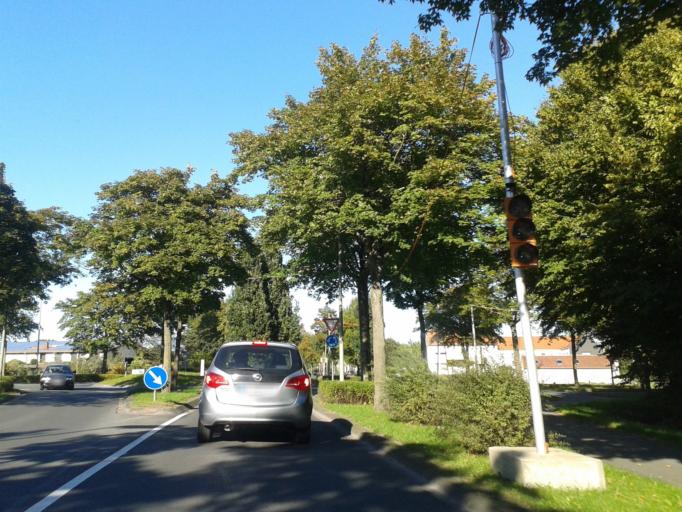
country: DE
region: North Rhine-Westphalia
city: Bad Lippspringe
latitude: 51.7707
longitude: 8.7987
